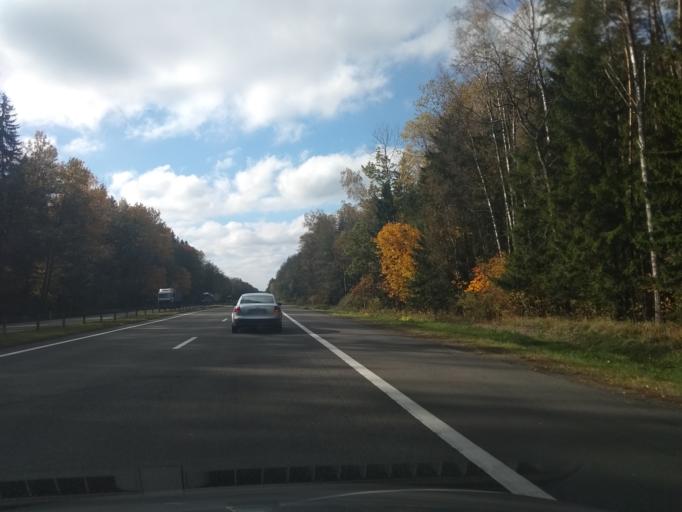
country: BY
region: Minsk
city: Enyerhyetykaw
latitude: 53.5772
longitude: 27.0147
